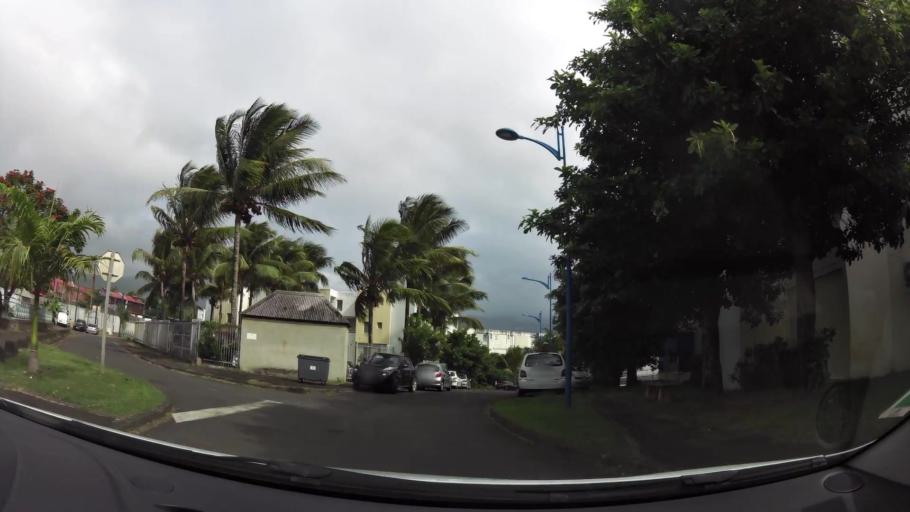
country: RE
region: Reunion
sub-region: Reunion
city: Sainte-Marie
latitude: -20.8994
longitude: 55.5557
